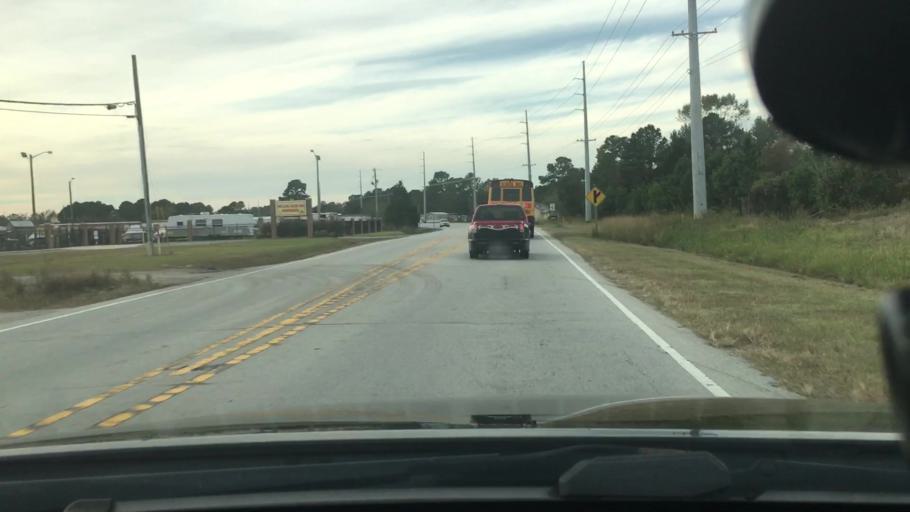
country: US
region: North Carolina
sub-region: Pitt County
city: Windsor
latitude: 35.5535
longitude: -77.3285
